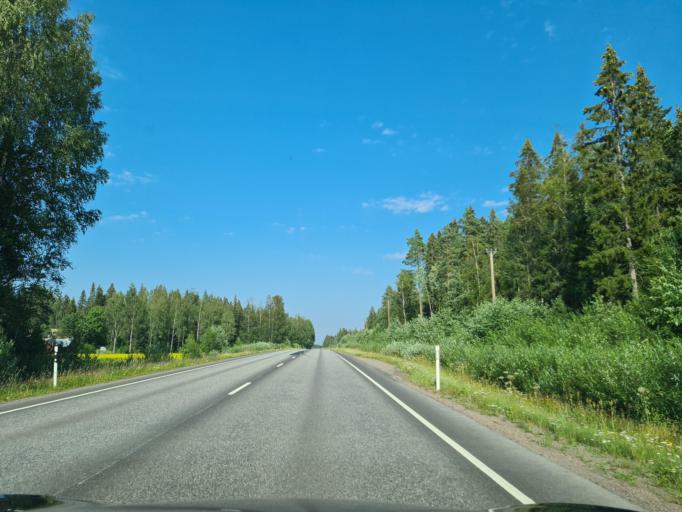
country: FI
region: Satakunta
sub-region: Pori
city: Laengelmaeki
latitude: 61.7749
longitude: 22.1853
